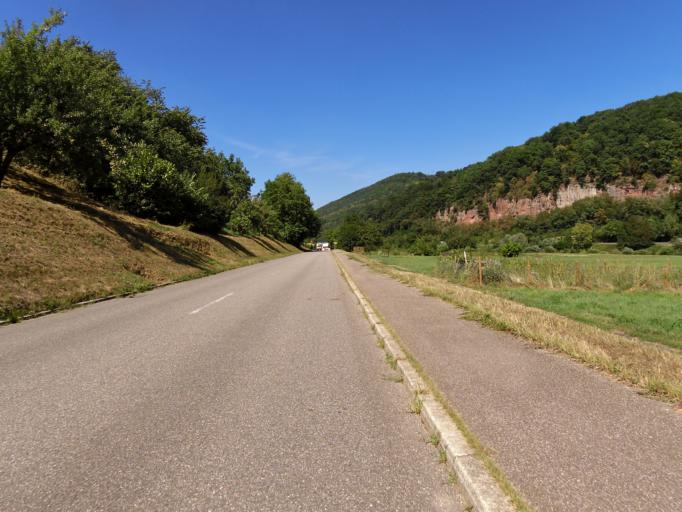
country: DE
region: Baden-Wuerttemberg
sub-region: Karlsruhe Region
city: Eberbach
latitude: 49.4424
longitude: 9.0036
